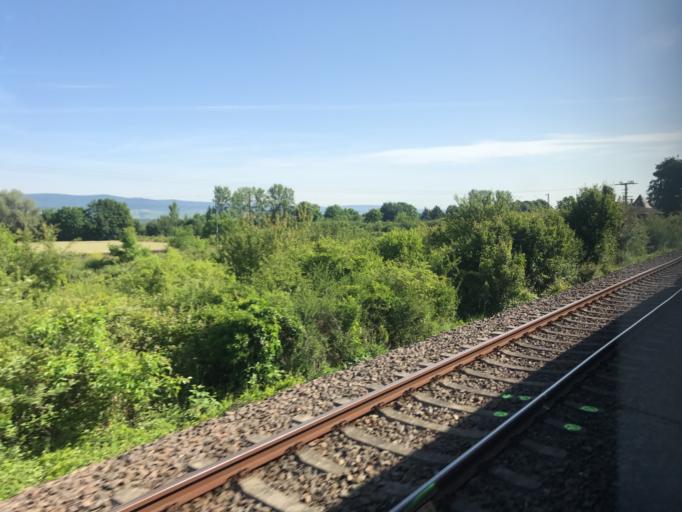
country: DE
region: Rheinland-Pfalz
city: Gau-Algesheim
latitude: 49.9571
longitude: 8.0042
